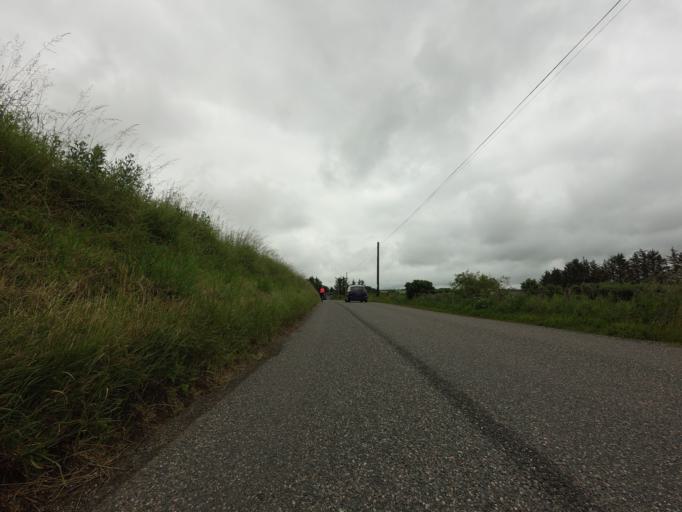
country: GB
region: Scotland
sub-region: Aberdeenshire
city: Turriff
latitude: 57.5372
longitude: -2.3720
